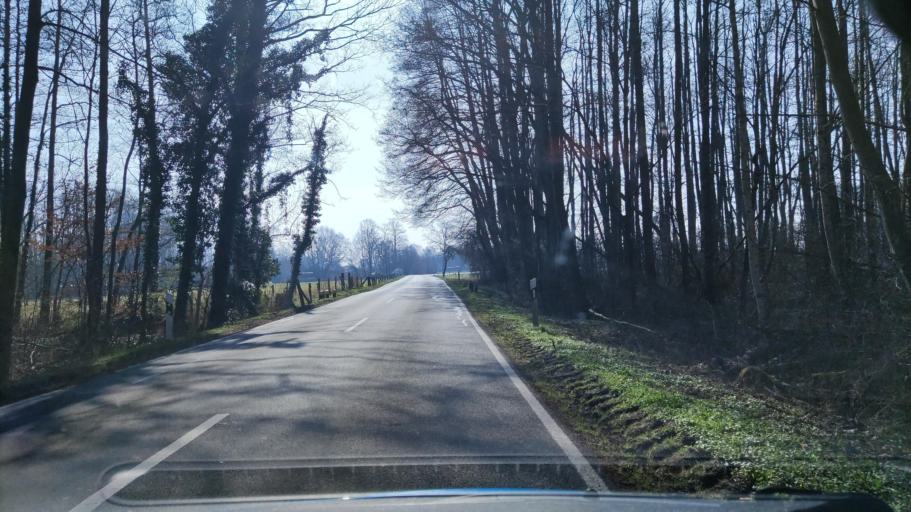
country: DE
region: Lower Saxony
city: Kusten
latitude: 52.9631
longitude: 11.0643
